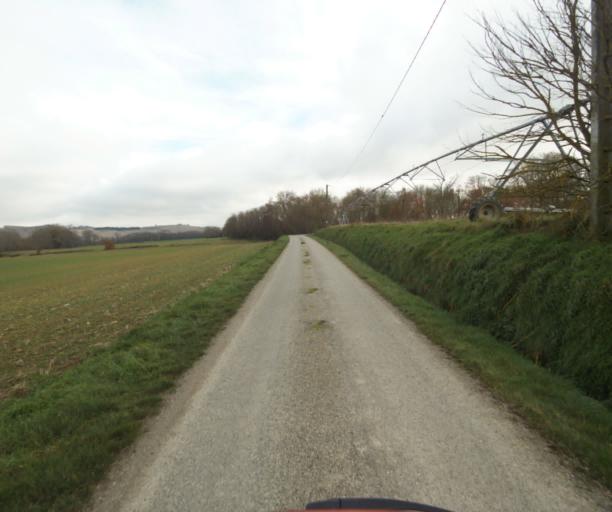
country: FR
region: Midi-Pyrenees
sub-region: Departement de l'Ariege
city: Mazeres
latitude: 43.2288
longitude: 1.7141
